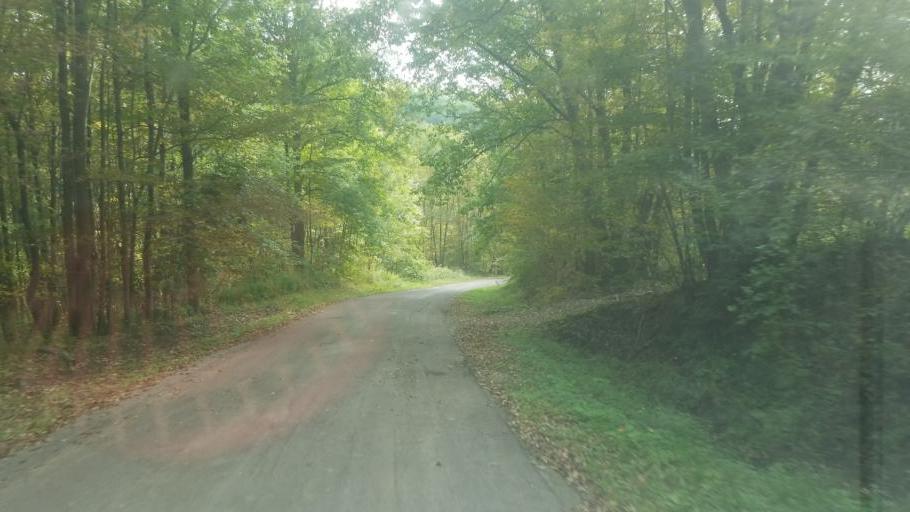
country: US
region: New York
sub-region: Allegany County
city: Cuba
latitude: 42.2263
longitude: -78.3459
